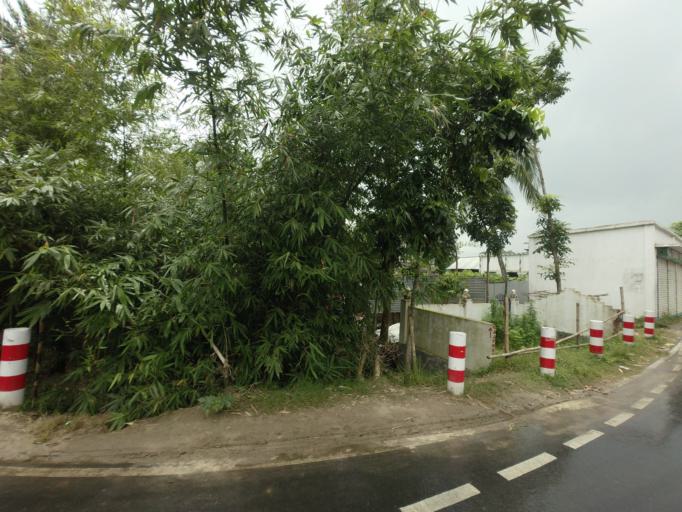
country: BD
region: Dhaka
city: Char Bhadrasan
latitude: 23.4116
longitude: 90.2151
